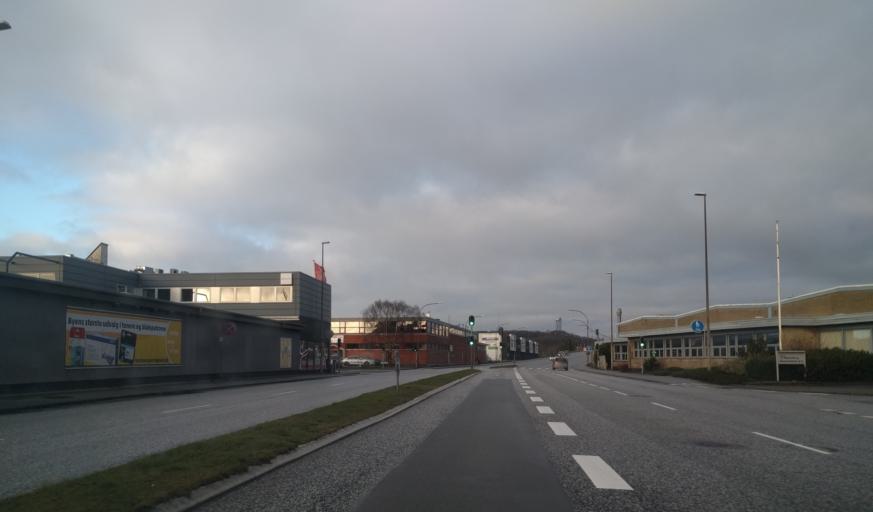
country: DK
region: North Denmark
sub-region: Alborg Kommune
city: Aalborg
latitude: 57.0379
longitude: 9.9282
